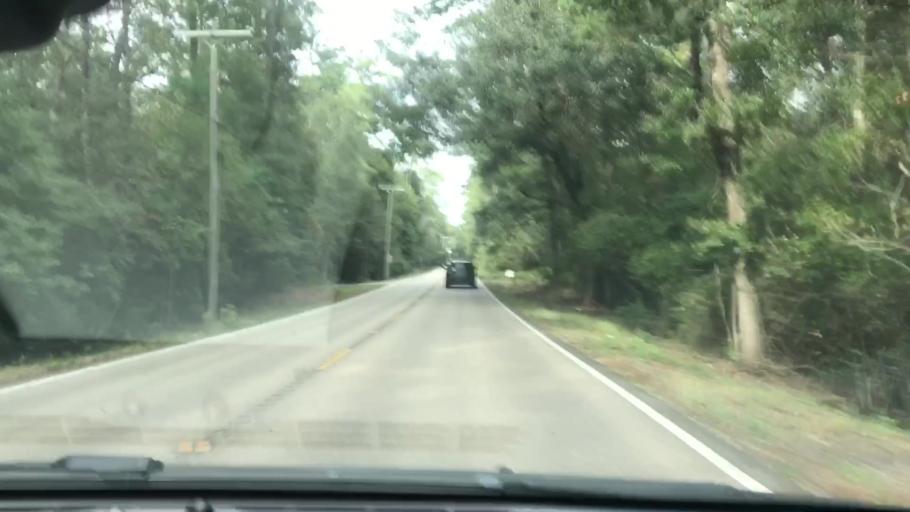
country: US
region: Louisiana
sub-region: Saint Tammany Parish
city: Abita Springs
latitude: 30.4827
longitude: -90.0265
